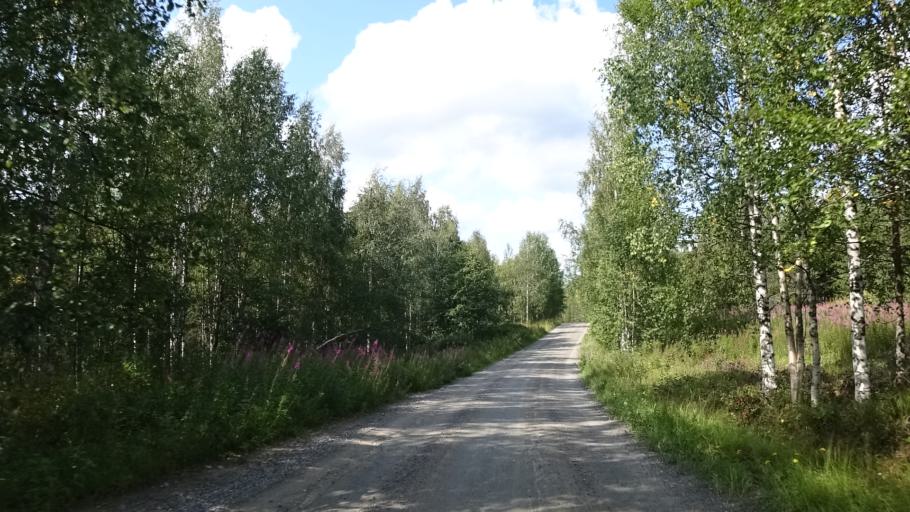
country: FI
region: North Karelia
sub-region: Joensuu
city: Ilomantsi
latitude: 62.9320
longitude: 31.3082
